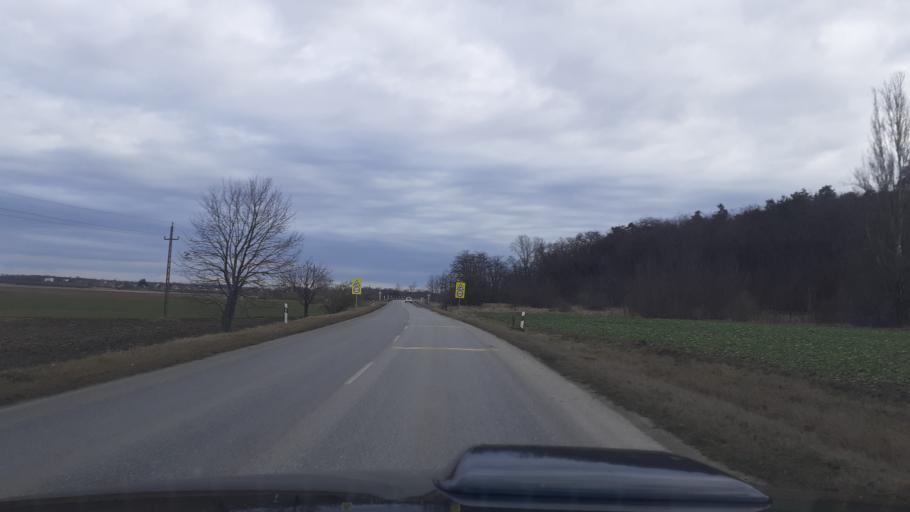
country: HU
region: Fejer
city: Seregelyes
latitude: 47.1232
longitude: 18.5572
